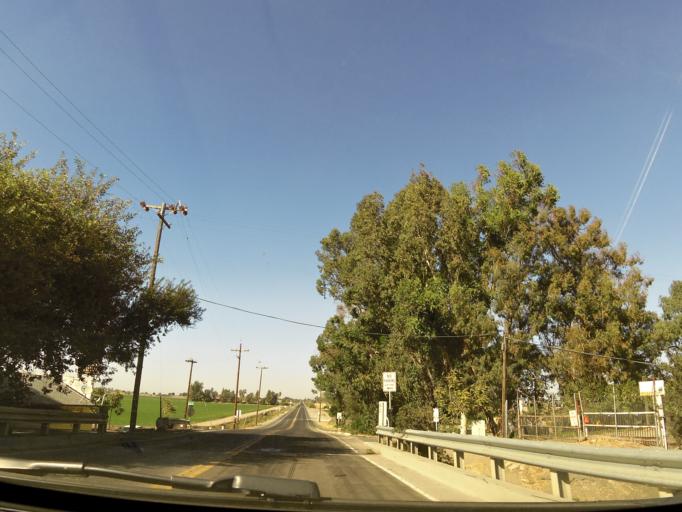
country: US
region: California
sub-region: San Joaquin County
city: Tracy
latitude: 37.8047
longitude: -121.4497
